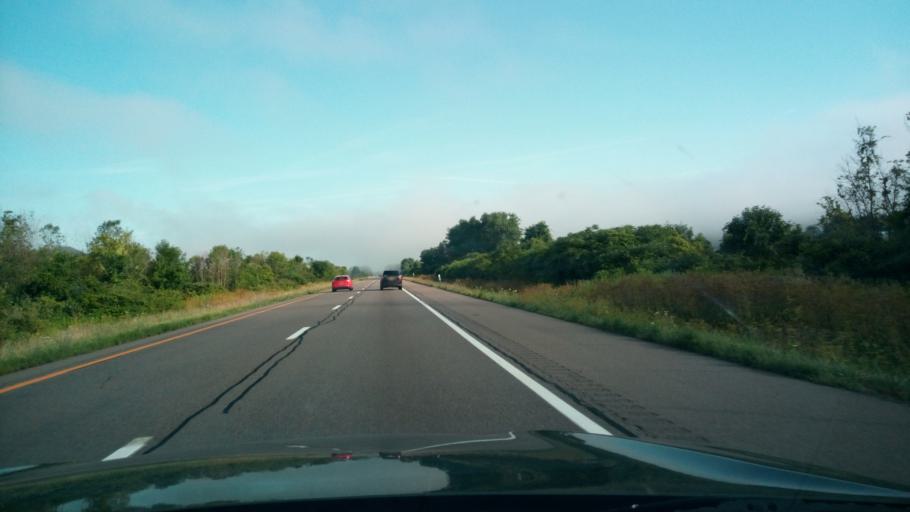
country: US
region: New York
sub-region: Steuben County
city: Gang Mills
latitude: 42.2488
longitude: -77.2021
